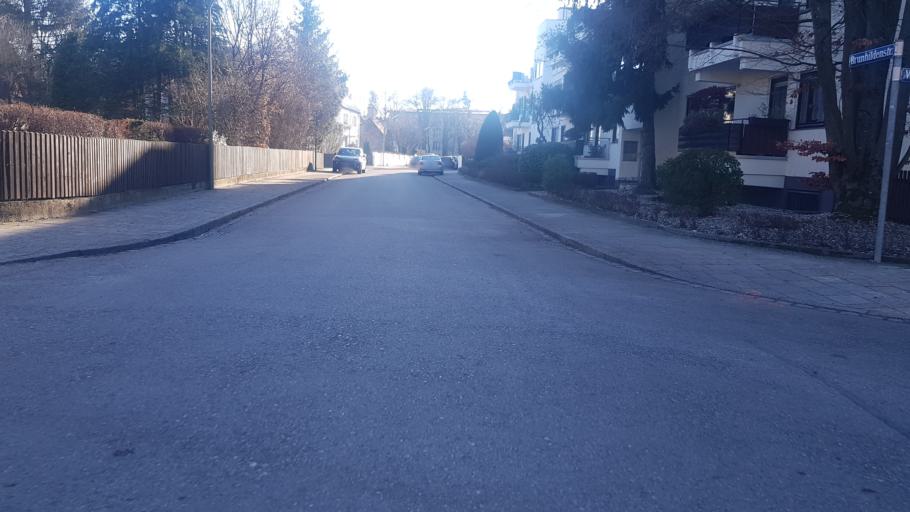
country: DE
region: Bavaria
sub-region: Upper Bavaria
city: Pasing
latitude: 48.1510
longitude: 11.5014
